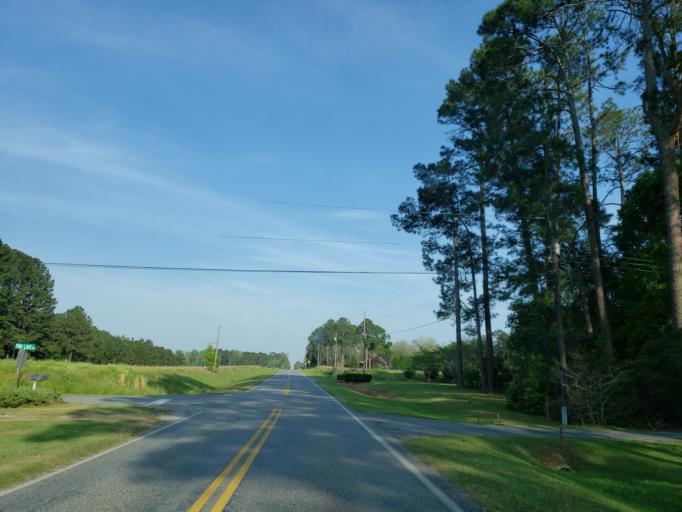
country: US
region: Georgia
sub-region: Tift County
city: Tifton
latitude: 31.4942
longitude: -83.5459
